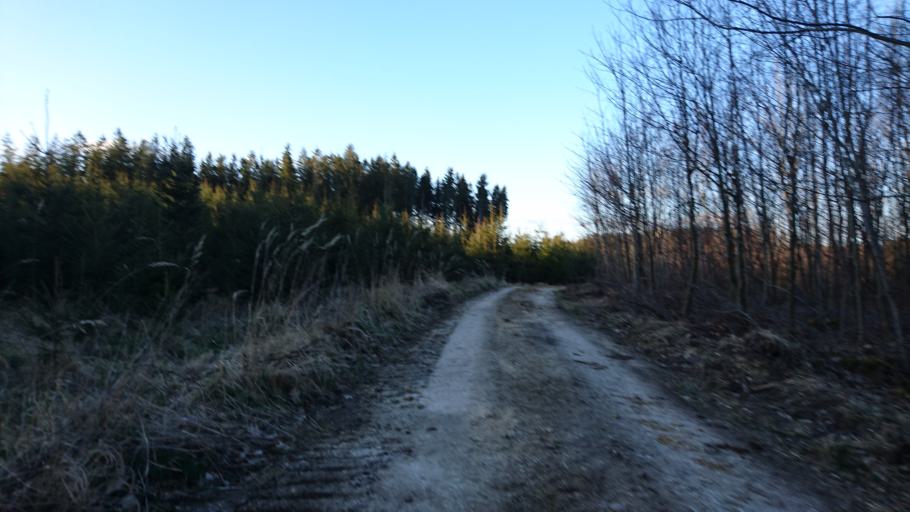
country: DE
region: Bavaria
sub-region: Swabia
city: Zusmarshausen
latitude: 48.4354
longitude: 10.6199
